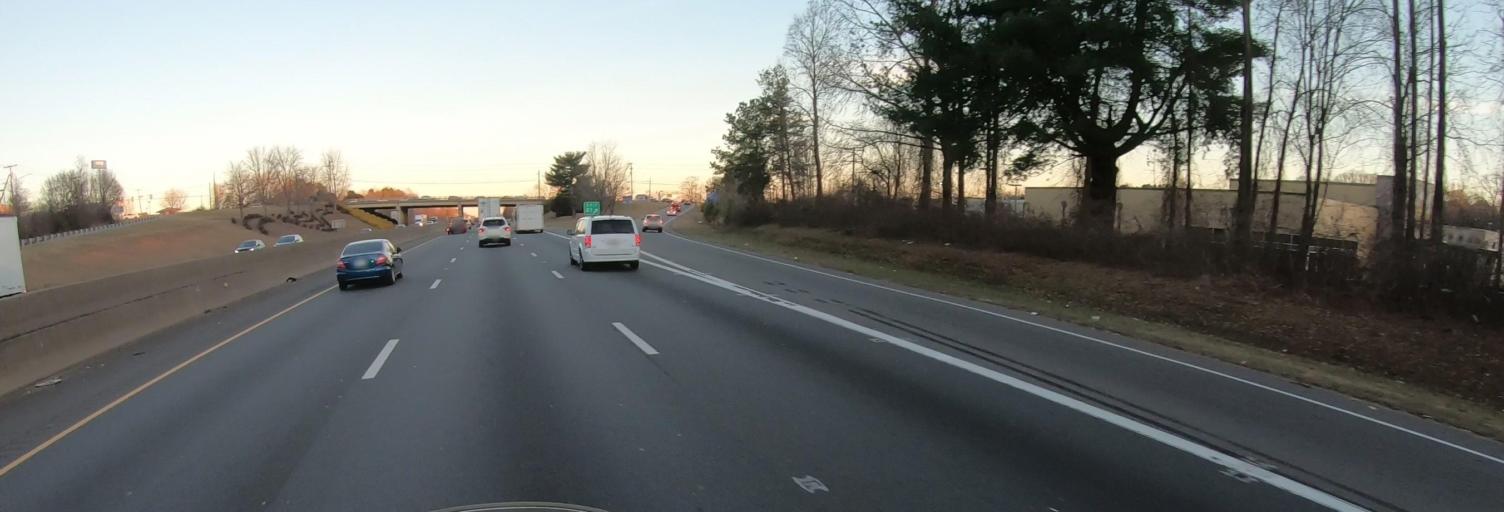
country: US
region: North Carolina
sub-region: Gaston County
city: Ranlo
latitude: 35.2665
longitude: -81.1356
